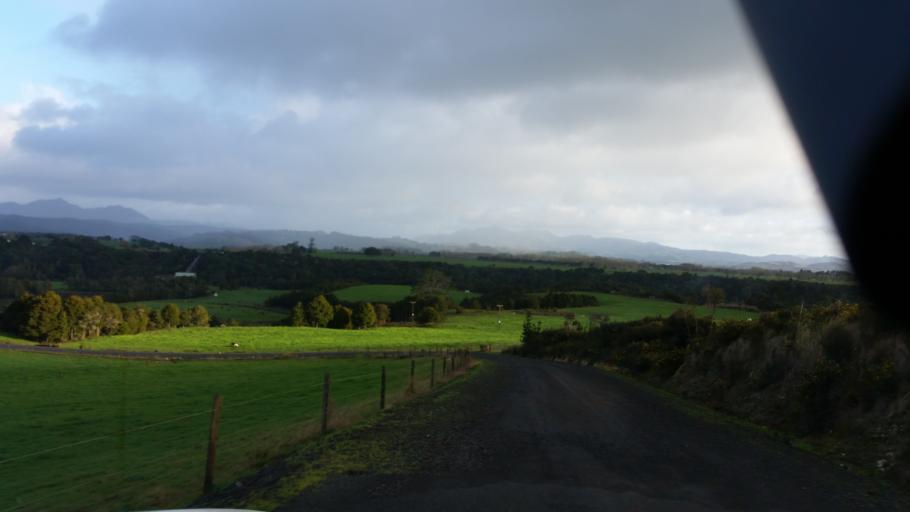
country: NZ
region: Northland
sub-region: Whangarei
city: Maungatapere
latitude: -35.7598
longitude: 174.0792
